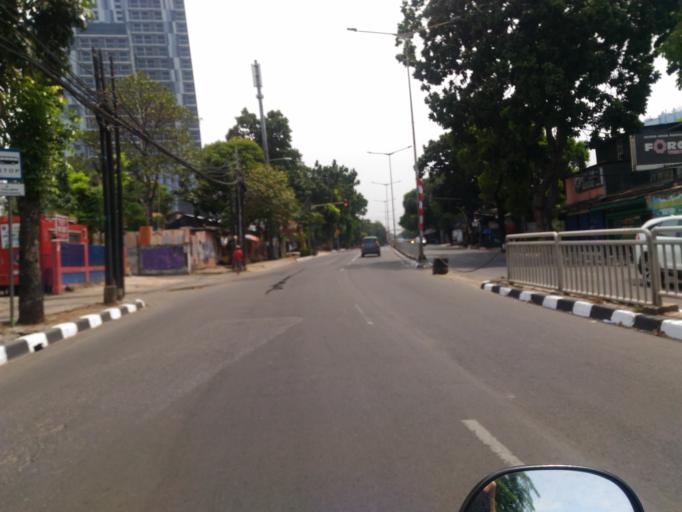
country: ID
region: Jakarta Raya
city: Jakarta
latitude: -6.2399
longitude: 106.8456
